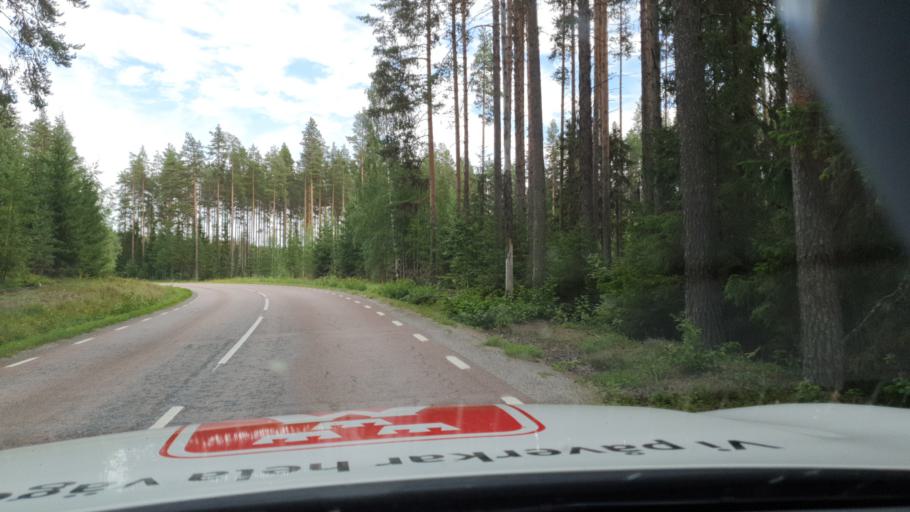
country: SE
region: Vaesternorrland
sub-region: Solleftea Kommun
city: As
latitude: 63.5707
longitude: 16.4194
